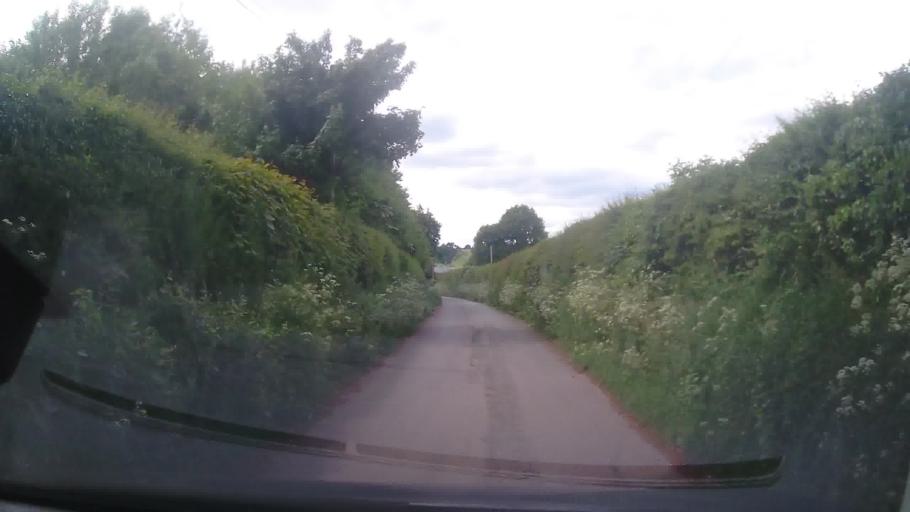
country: GB
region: England
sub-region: Shropshire
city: Clive
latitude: 52.8093
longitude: -2.7343
